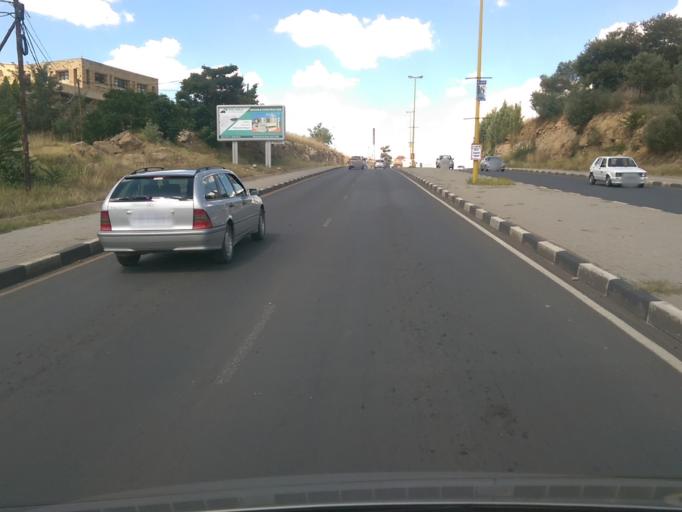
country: LS
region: Maseru
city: Maseru
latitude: -29.3172
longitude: 27.4840
